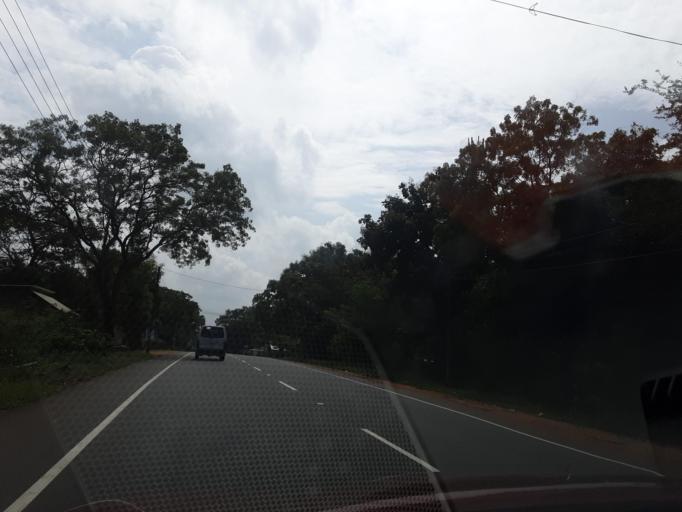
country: LK
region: North Central
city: Anuradhapura
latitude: 8.4913
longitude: 80.5116
